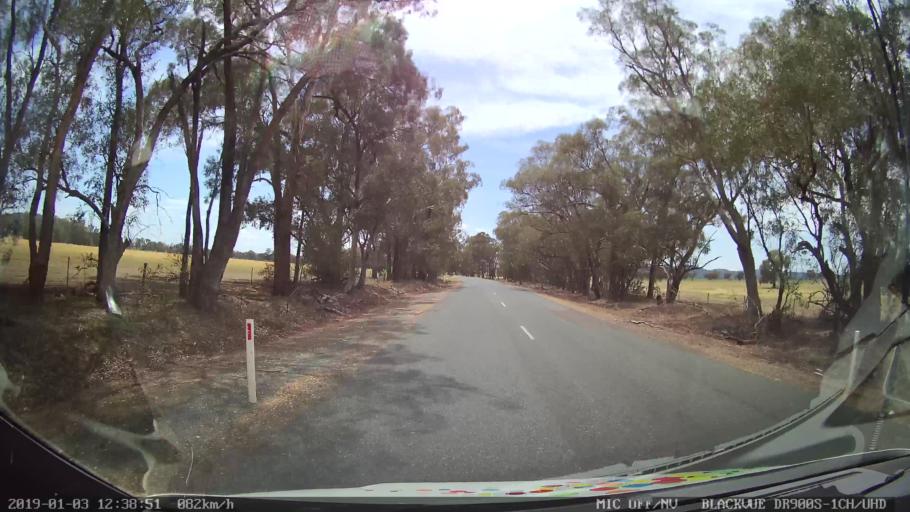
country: AU
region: New South Wales
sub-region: Weddin
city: Grenfell
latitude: -33.8302
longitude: 148.2006
